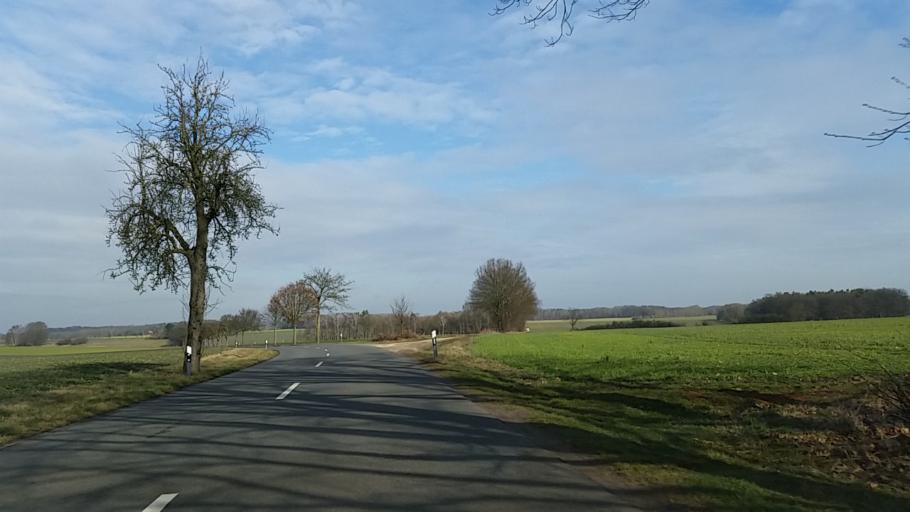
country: DE
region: Lower Saxony
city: Altenmedingen
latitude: 53.1505
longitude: 10.6192
